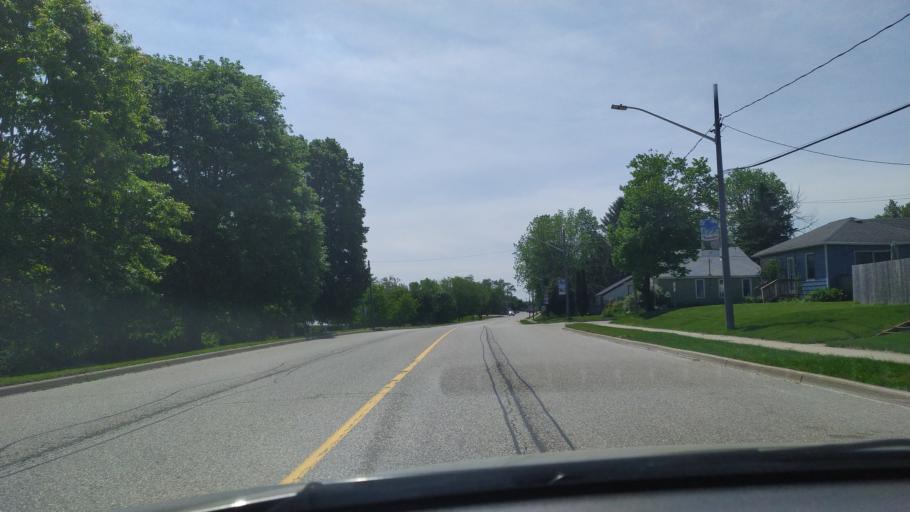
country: CA
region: Ontario
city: Dorchester
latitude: 43.0624
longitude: -80.9983
